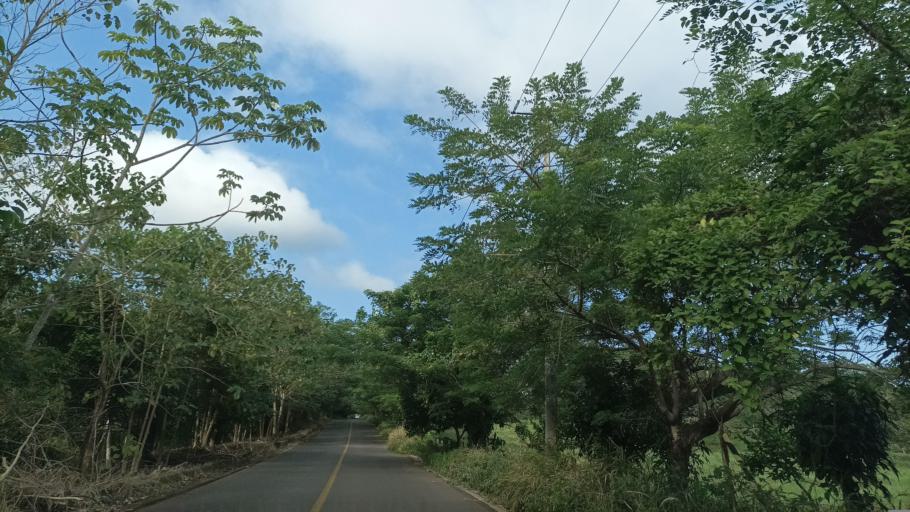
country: MX
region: Veracruz
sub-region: Pajapan
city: Pajapan
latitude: 18.1857
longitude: -94.6847
